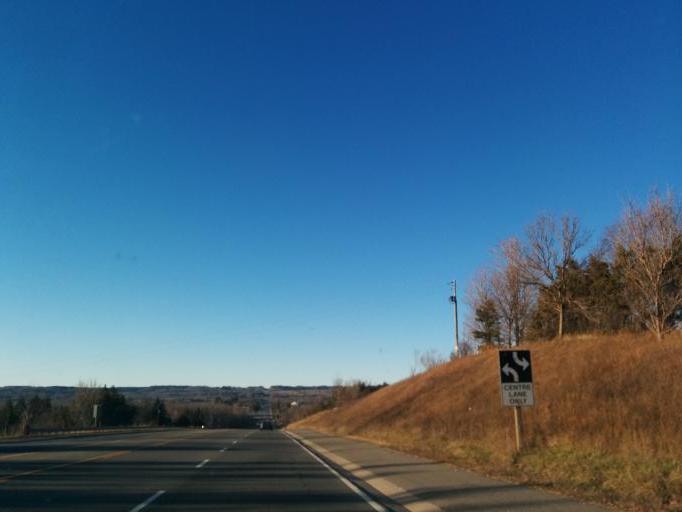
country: CA
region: Ontario
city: Brampton
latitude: 43.8060
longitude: -79.9224
